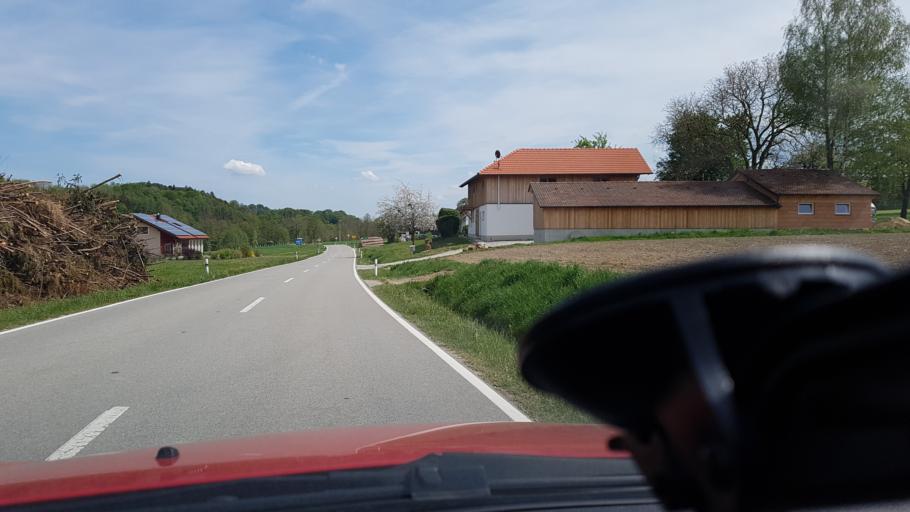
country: DE
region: Bavaria
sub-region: Lower Bavaria
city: Stubenberg
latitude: 48.3364
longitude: 13.0909
